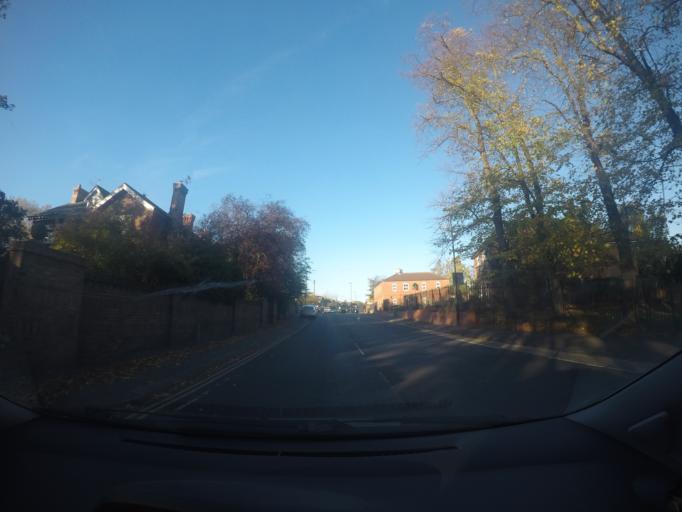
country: GB
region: England
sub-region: City of York
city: York
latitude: 53.9750
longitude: -1.0734
